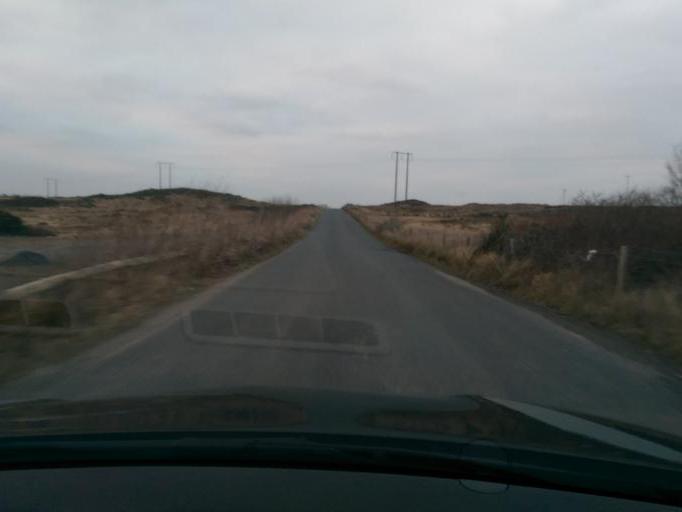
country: IE
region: Connaught
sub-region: County Galway
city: Bearna
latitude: 53.2803
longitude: -9.1631
